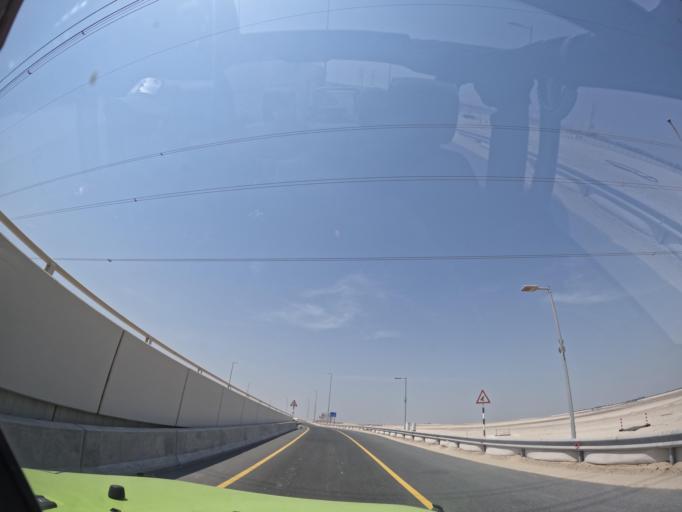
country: AE
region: Abu Dhabi
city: Abu Dhabi
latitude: 24.1650
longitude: 54.3532
